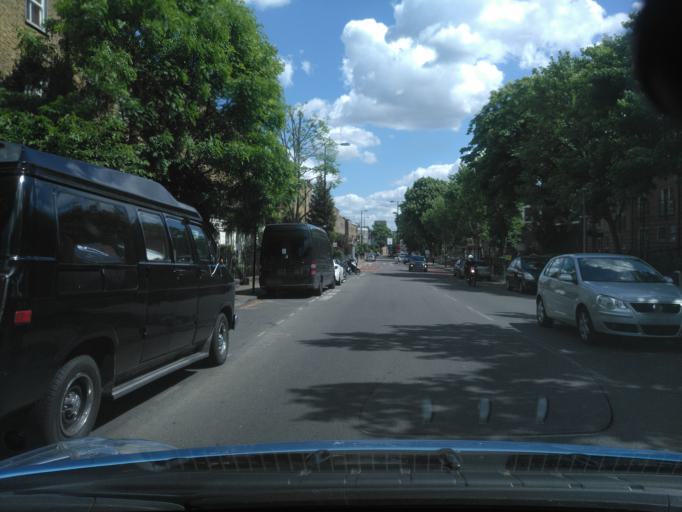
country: GB
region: England
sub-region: Greater London
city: Islington
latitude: 51.5471
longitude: -0.0913
